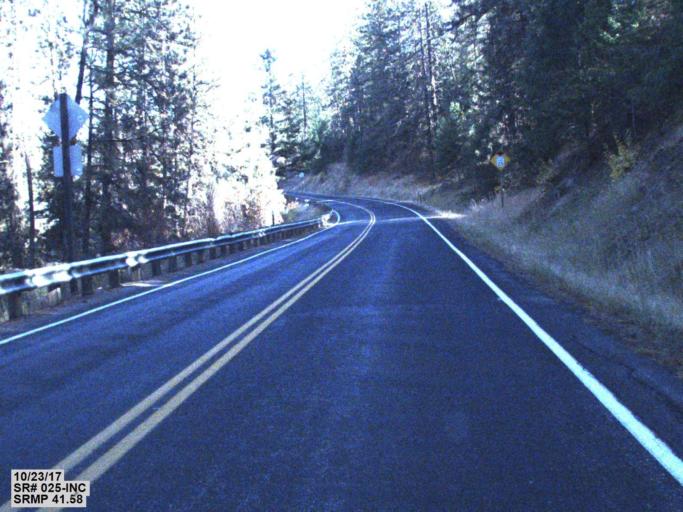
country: US
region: Washington
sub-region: Lincoln County
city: Davenport
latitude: 48.1170
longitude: -118.1970
